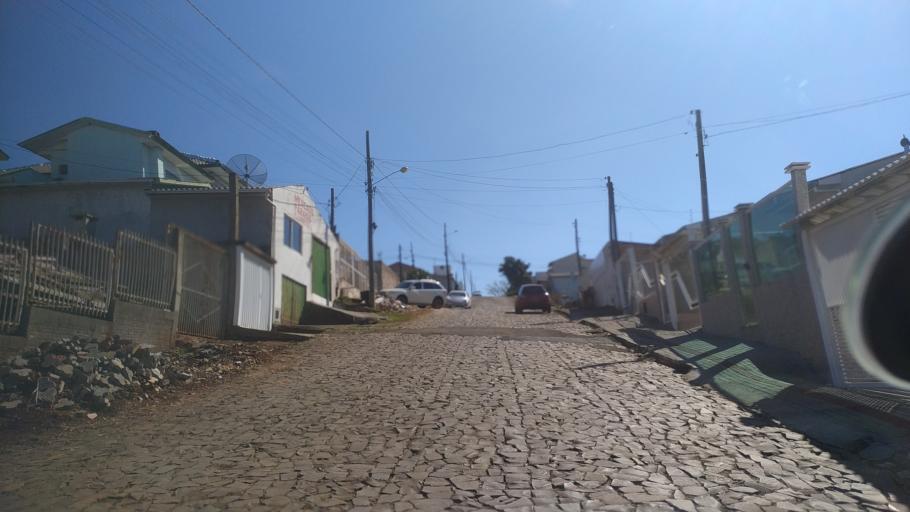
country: BR
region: Santa Catarina
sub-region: Chapeco
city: Chapeco
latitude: -27.0907
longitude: -52.5864
